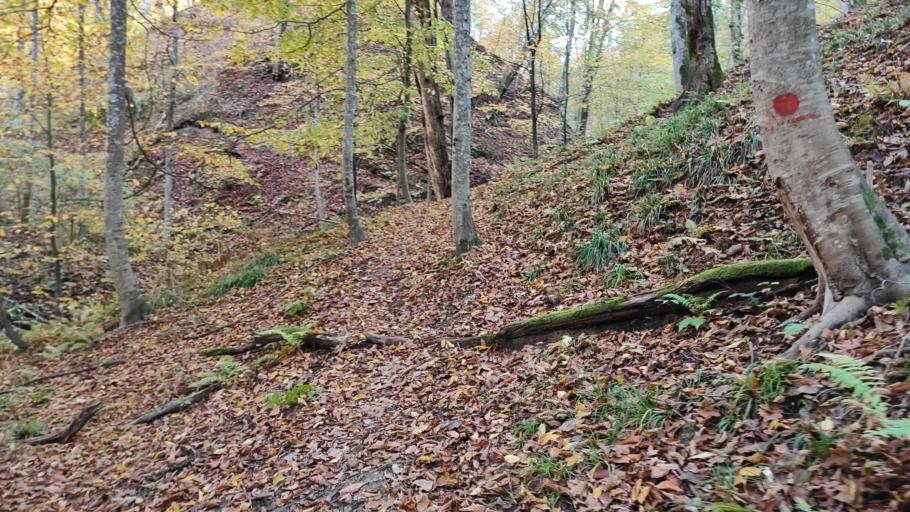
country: RU
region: Krasnodarskiy
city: Goryachiy Klyuch
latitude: 44.5978
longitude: 39.1219
